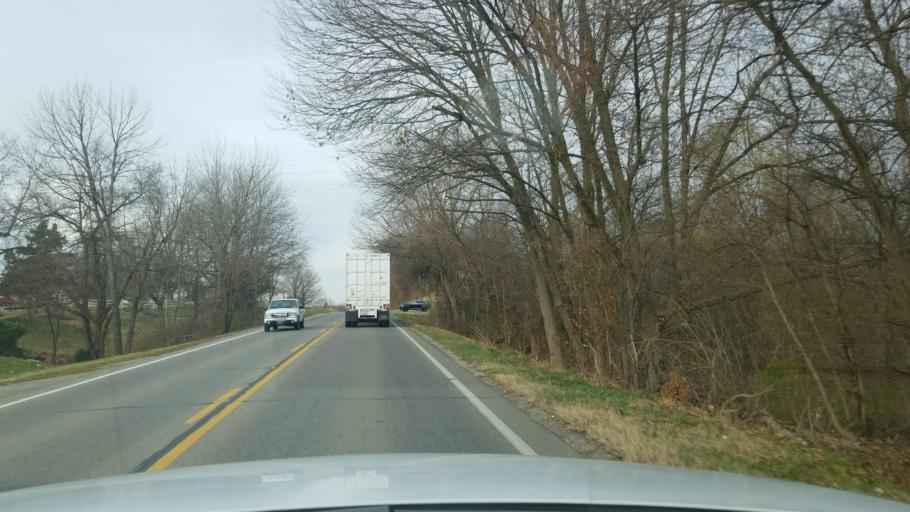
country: US
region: Indiana
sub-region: Posey County
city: Mount Vernon
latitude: 37.9291
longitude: -87.9341
